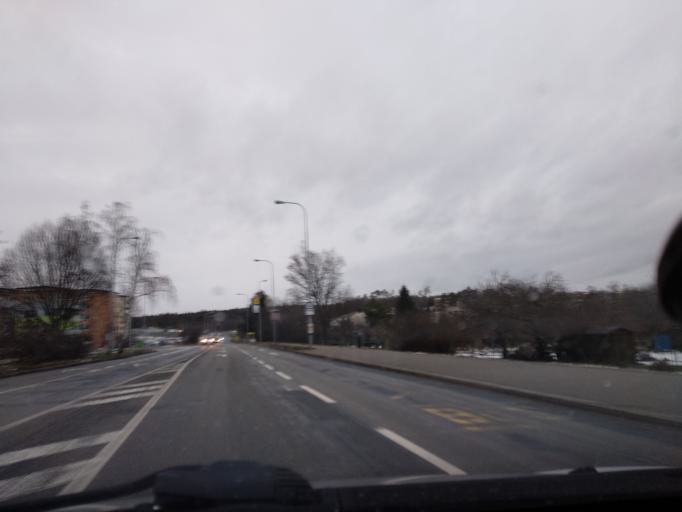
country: CZ
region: South Moravian
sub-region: Mesto Brno
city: Brno
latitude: 49.2338
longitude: 16.6293
